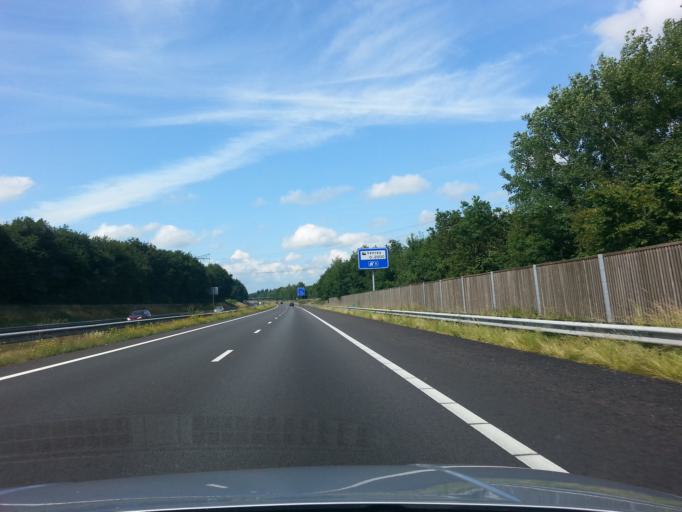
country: NL
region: Limburg
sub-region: Gemeente Venray
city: Venray
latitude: 51.5314
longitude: 6.0000
